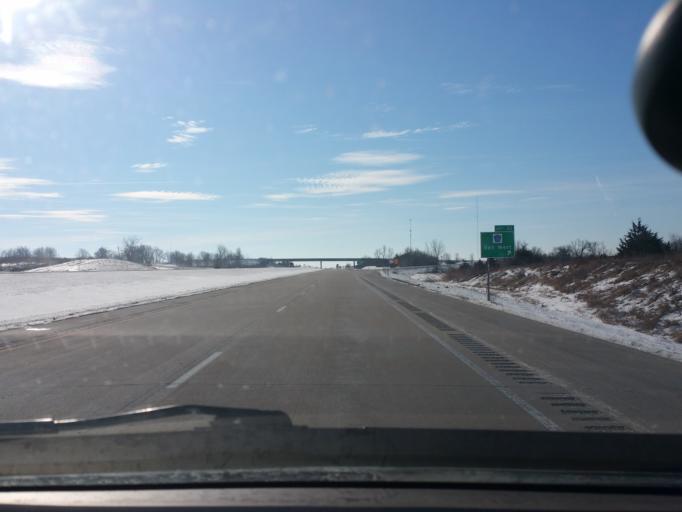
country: US
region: Iowa
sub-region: Decatur County
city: Leon
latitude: 40.8757
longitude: -93.8022
